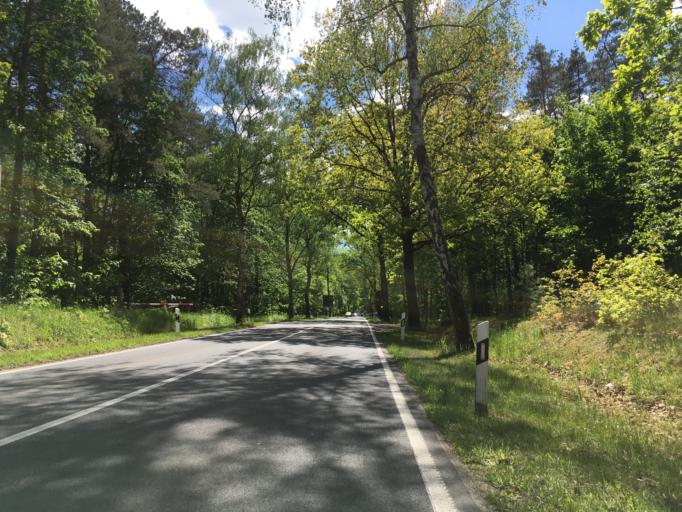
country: DE
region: Brandenburg
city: Rudnitz
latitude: 52.7706
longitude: 13.5647
